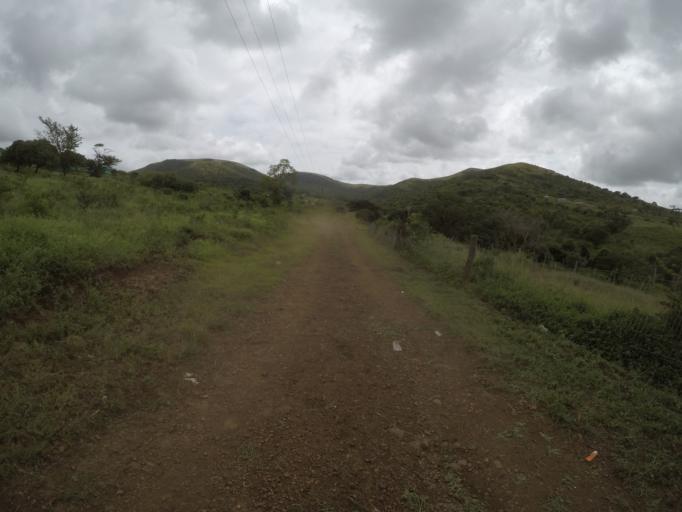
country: ZA
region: KwaZulu-Natal
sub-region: uThungulu District Municipality
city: Empangeni
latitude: -28.5866
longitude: 31.8889
